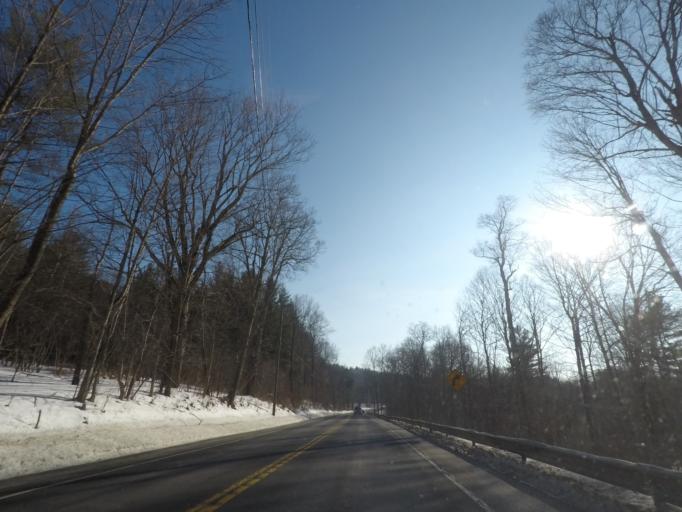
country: US
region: Massachusetts
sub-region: Berkshire County
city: Richmond
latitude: 42.5061
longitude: -73.3674
